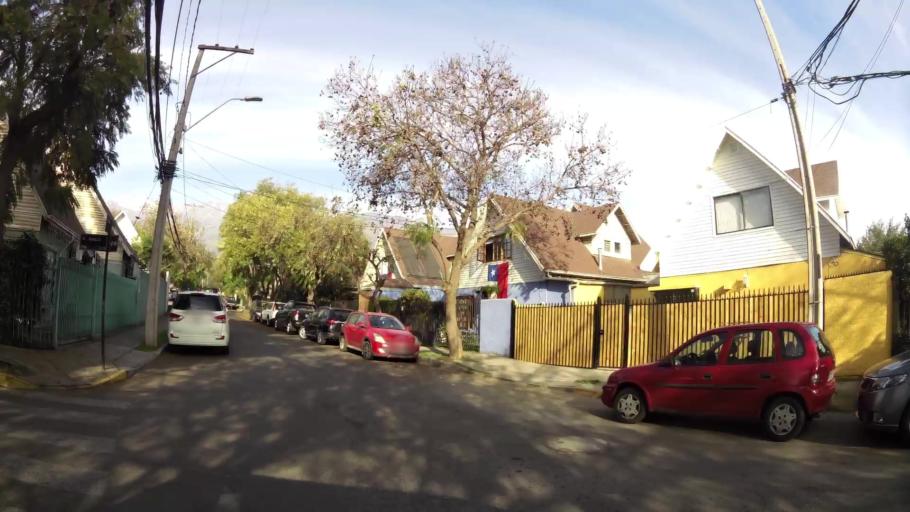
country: CL
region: Santiago Metropolitan
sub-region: Provincia de Santiago
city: Villa Presidente Frei, Nunoa, Santiago, Chile
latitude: -33.5101
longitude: -70.5582
